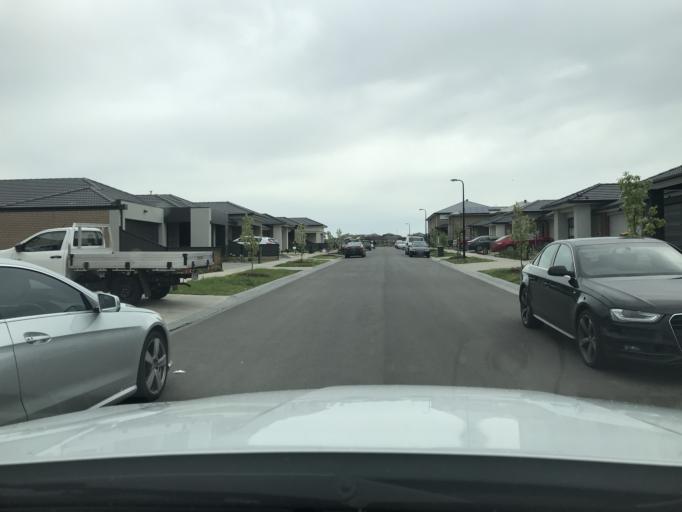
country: AU
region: Victoria
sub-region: Hume
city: Roxburgh Park
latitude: -37.6038
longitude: 144.9101
